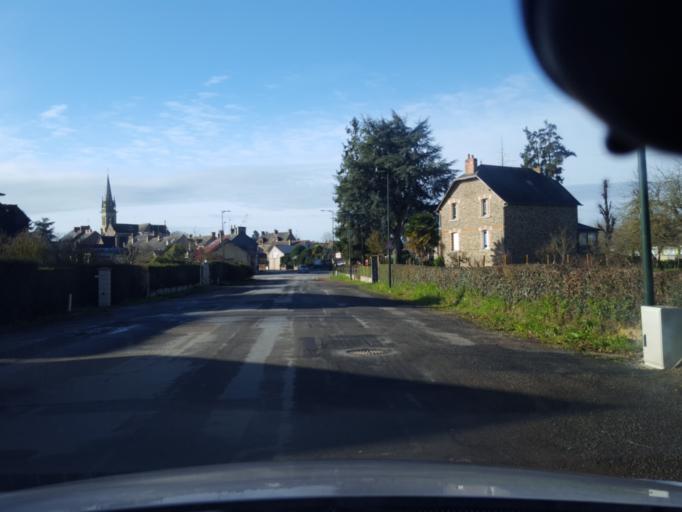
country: FR
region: Brittany
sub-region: Departement d'Ille-et-Vilaine
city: Guignen
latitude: 47.9225
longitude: -1.8583
